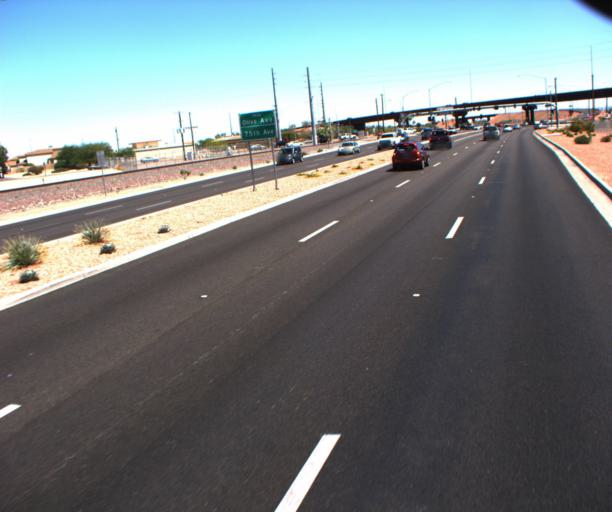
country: US
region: Arizona
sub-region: Maricopa County
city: Peoria
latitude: 33.5681
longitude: -112.2220
